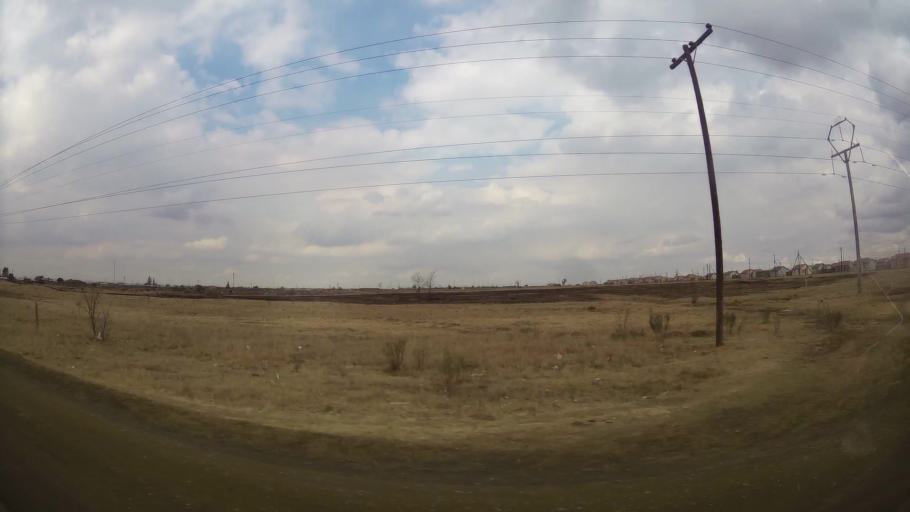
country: ZA
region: Orange Free State
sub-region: Fezile Dabi District Municipality
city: Sasolburg
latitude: -26.8560
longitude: 27.8661
